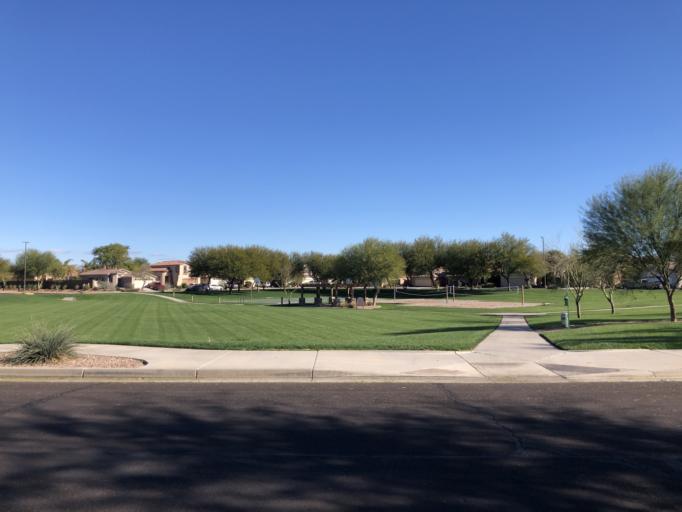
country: US
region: Arizona
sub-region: Maricopa County
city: Queen Creek
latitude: 33.2716
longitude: -111.7032
